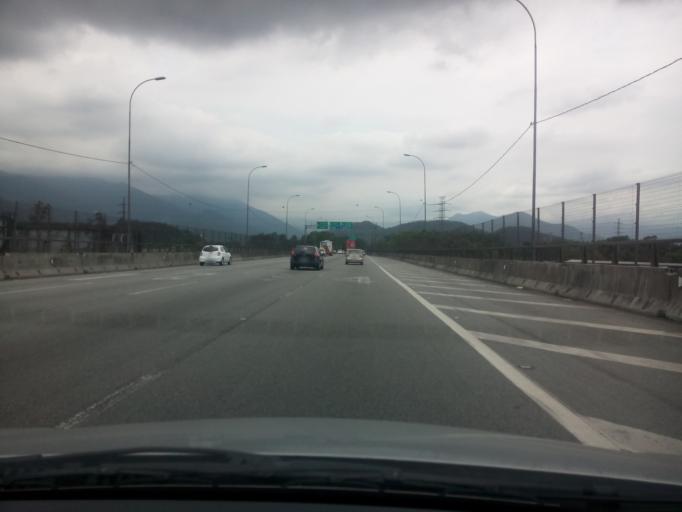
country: BR
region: Sao Paulo
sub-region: Cubatao
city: Cubatao
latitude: -23.8894
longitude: -46.4338
